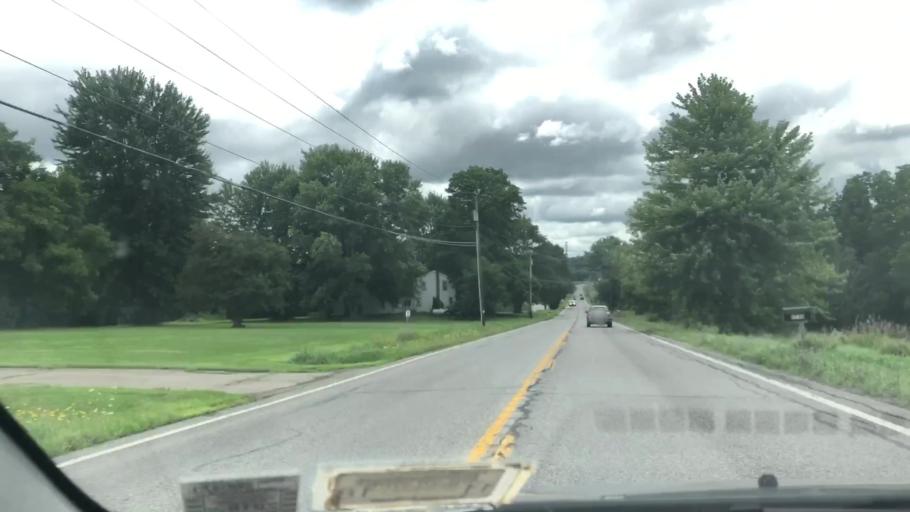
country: US
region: New York
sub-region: Wayne County
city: Macedon
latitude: 43.1059
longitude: -77.2929
